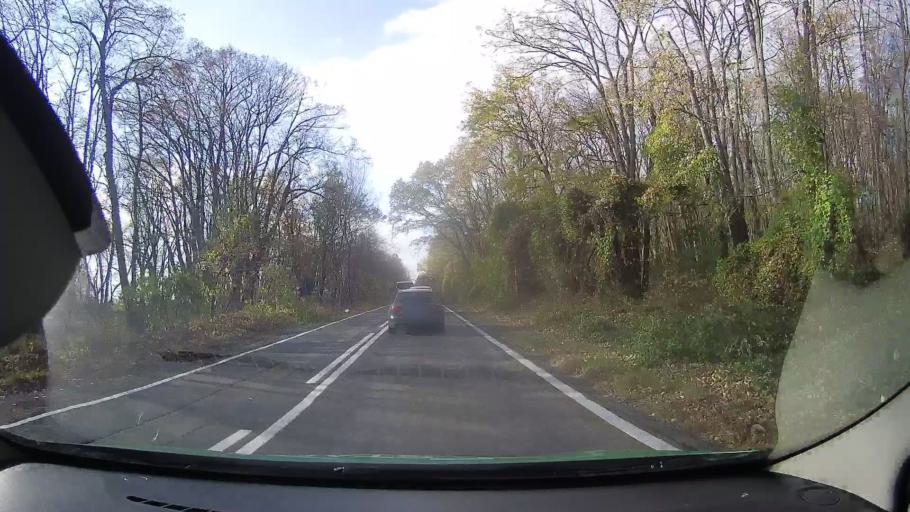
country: RO
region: Tulcea
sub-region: Comuna Topolog
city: Topolog
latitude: 44.9070
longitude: 28.4118
